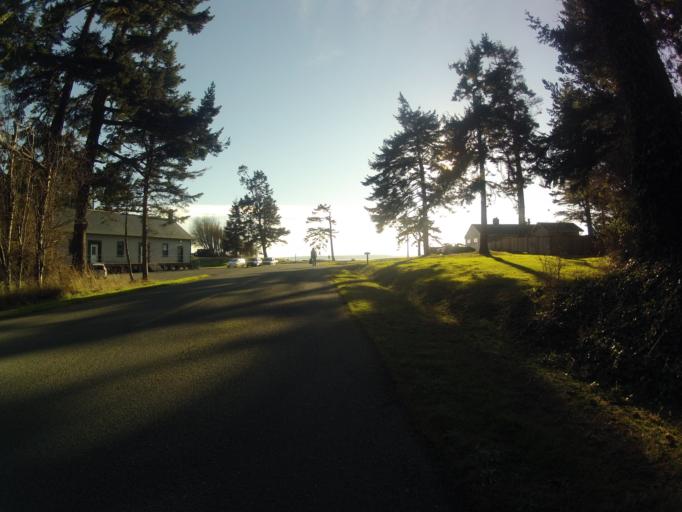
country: US
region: Washington
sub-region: Island County
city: Coupeville
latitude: 48.1592
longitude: -122.6765
